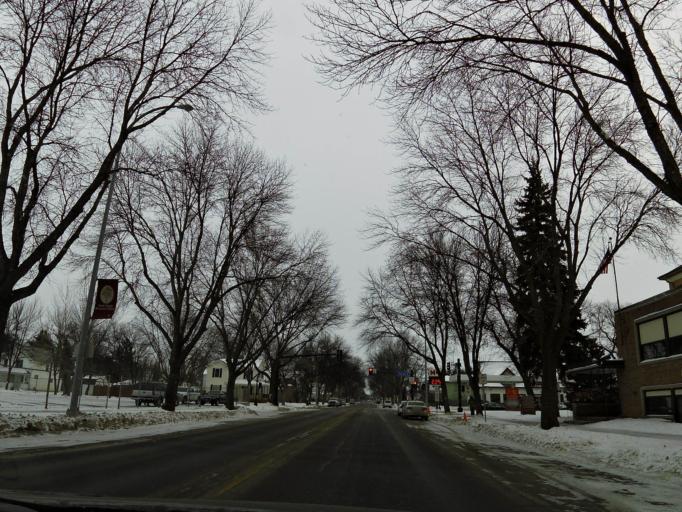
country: US
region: North Dakota
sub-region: Grand Forks County
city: Grand Forks
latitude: 47.9275
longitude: -97.0393
